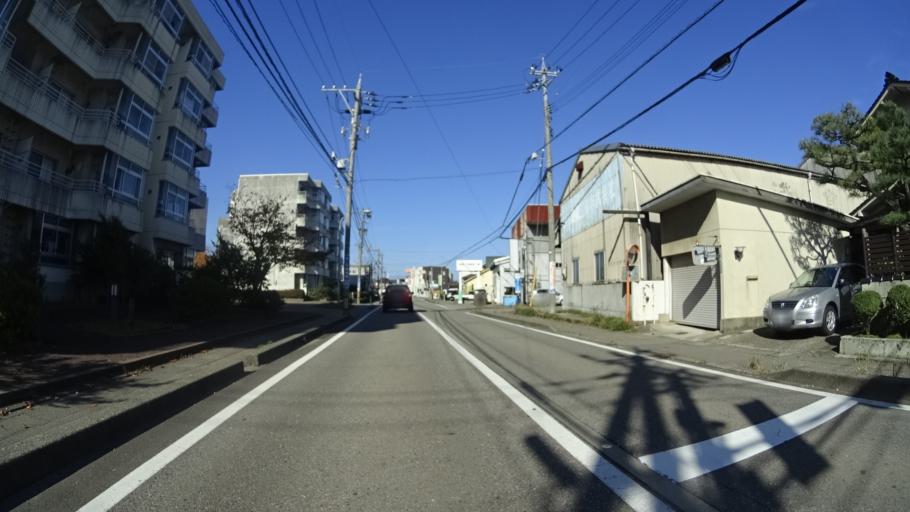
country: JP
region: Ishikawa
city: Kanazawa-shi
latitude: 36.5989
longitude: 136.6085
